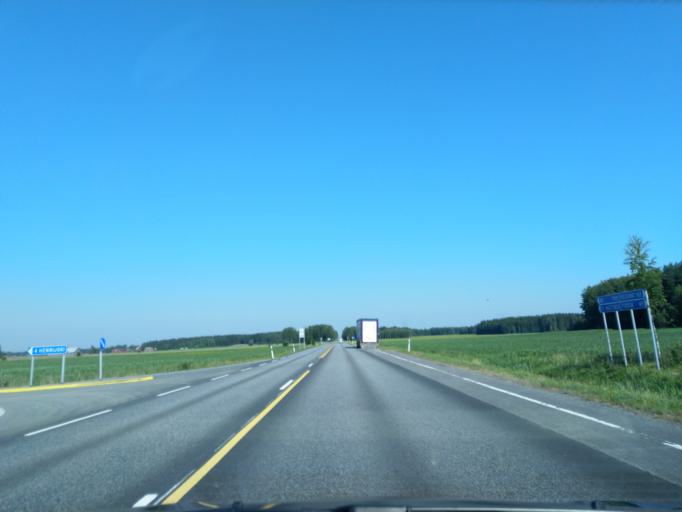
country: FI
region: Varsinais-Suomi
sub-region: Loimaa
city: Alastaro
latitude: 61.0620
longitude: 22.9376
